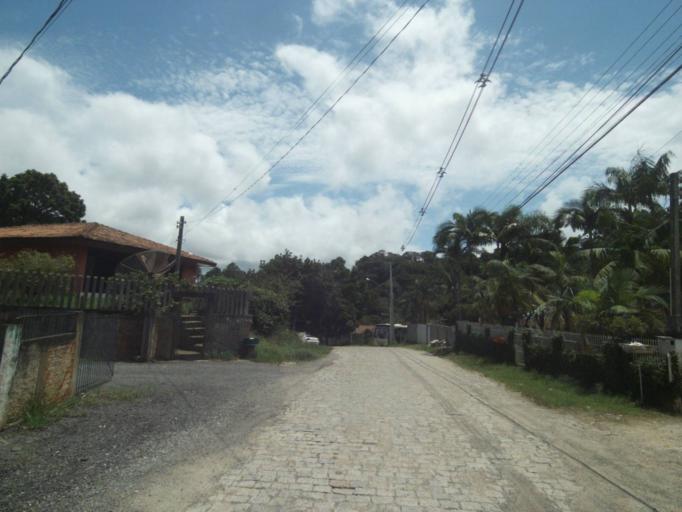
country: BR
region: Parana
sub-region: Campina Grande Do Sul
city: Campina Grande do Sul
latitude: -25.1109
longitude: -48.8353
